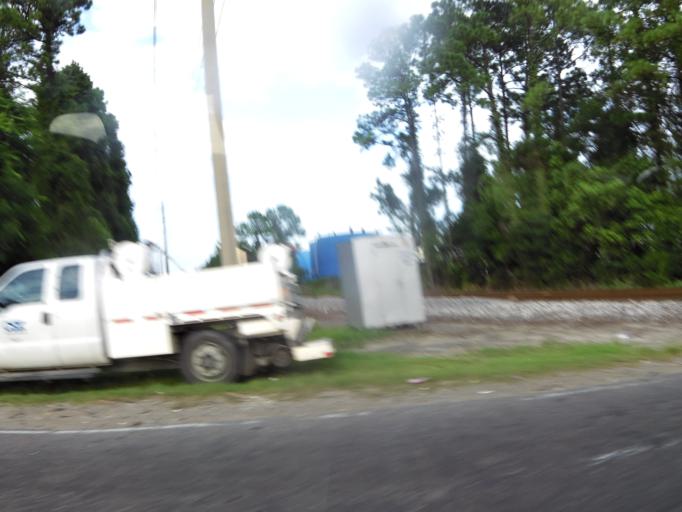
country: US
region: Florida
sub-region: Duval County
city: Jacksonville
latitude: 30.3482
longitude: -81.7521
